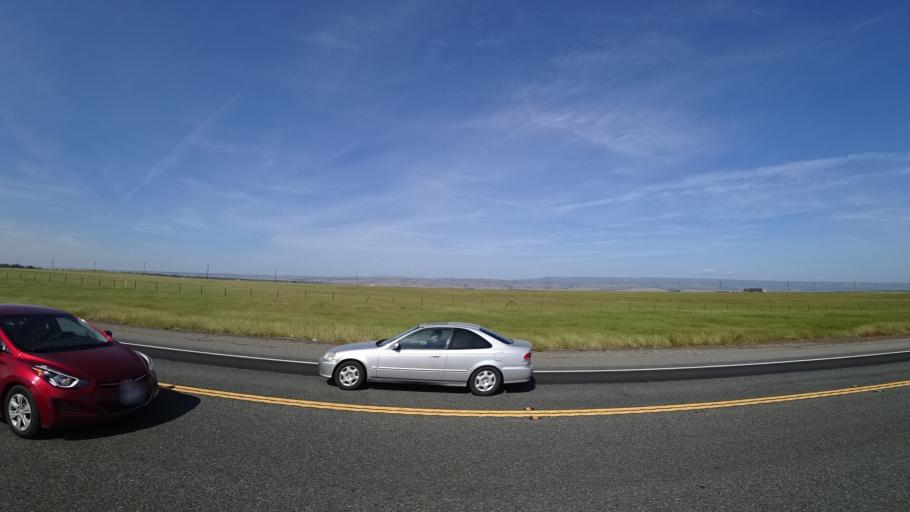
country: US
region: California
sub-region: Tehama County
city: Los Molinos
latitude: 39.9183
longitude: -122.0175
